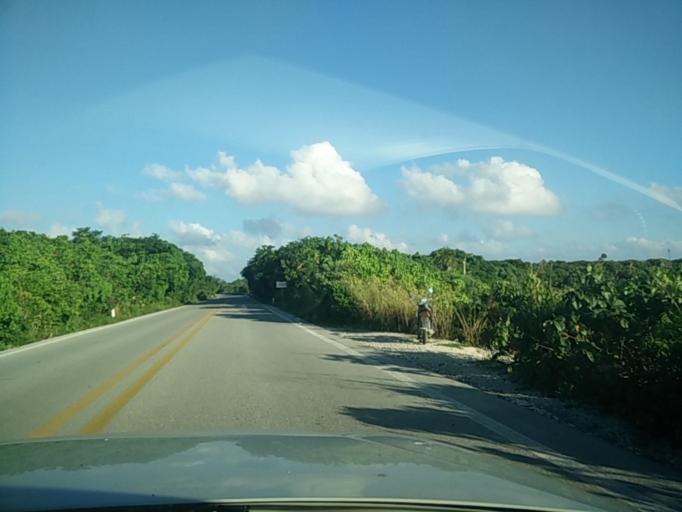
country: MX
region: Quintana Roo
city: San Miguel de Cozumel
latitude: 20.3471
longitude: -86.9020
